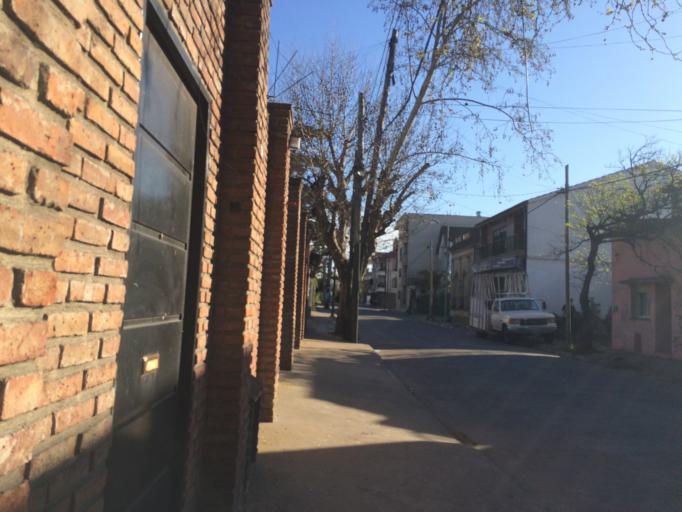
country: AR
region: Buenos Aires
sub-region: Partido de Lomas de Zamora
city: Lomas de Zamora
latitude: -34.7787
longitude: -58.3980
